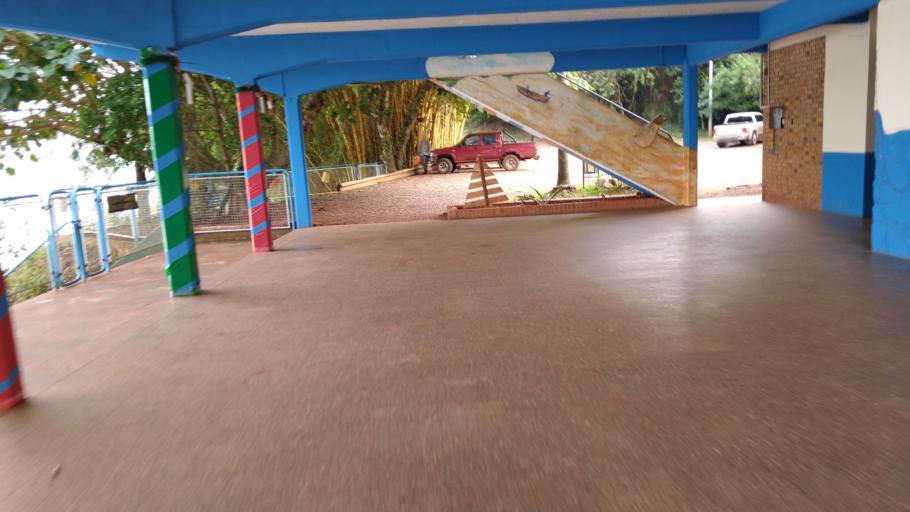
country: AR
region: Misiones
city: Caraguatay
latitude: -26.5699
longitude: -54.7980
